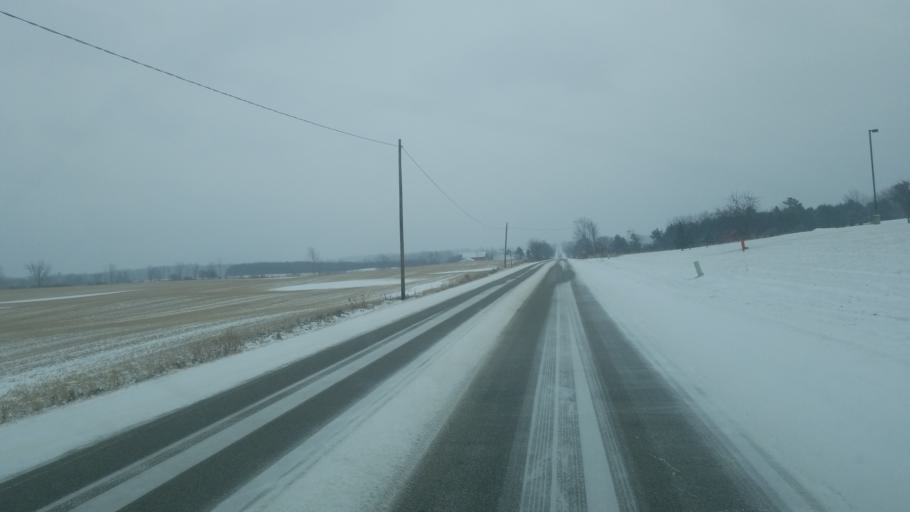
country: US
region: Michigan
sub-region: Osceola County
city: Evart
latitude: 44.1025
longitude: -85.1324
